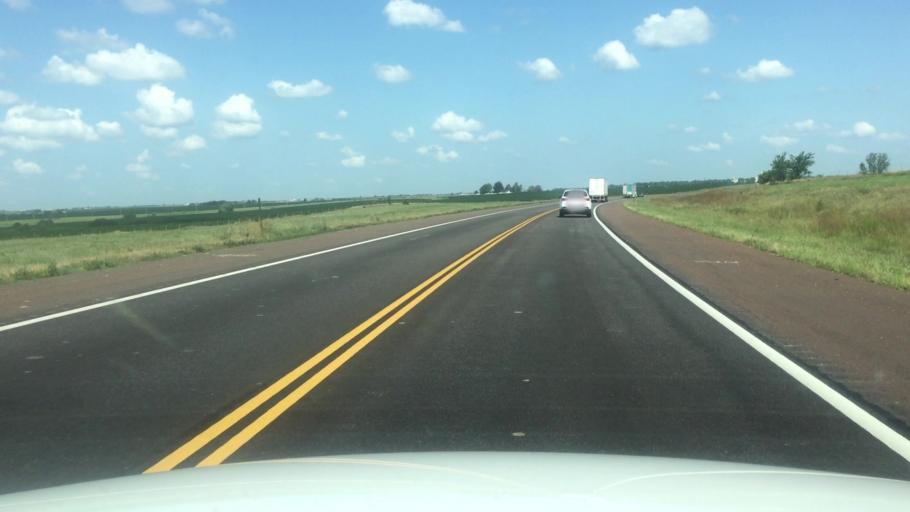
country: US
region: Kansas
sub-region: Nemaha County
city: Sabetha
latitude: 39.8691
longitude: -95.7763
